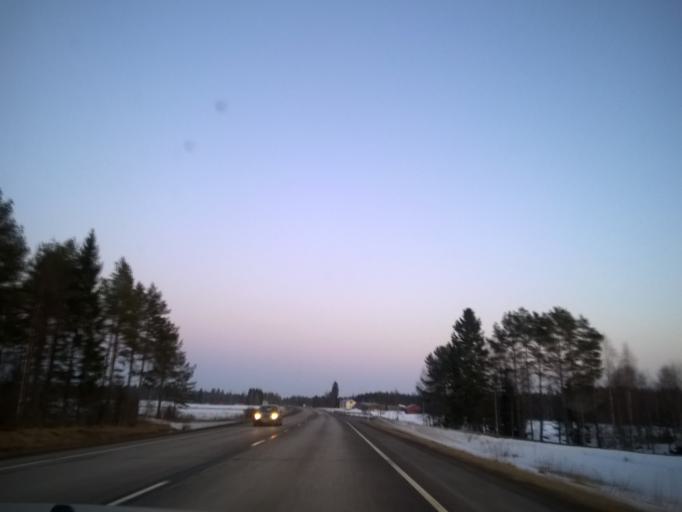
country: FI
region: Northern Ostrobothnia
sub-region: Nivala-Haapajaervi
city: Pyhaejaervi
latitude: 63.8160
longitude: 25.8981
